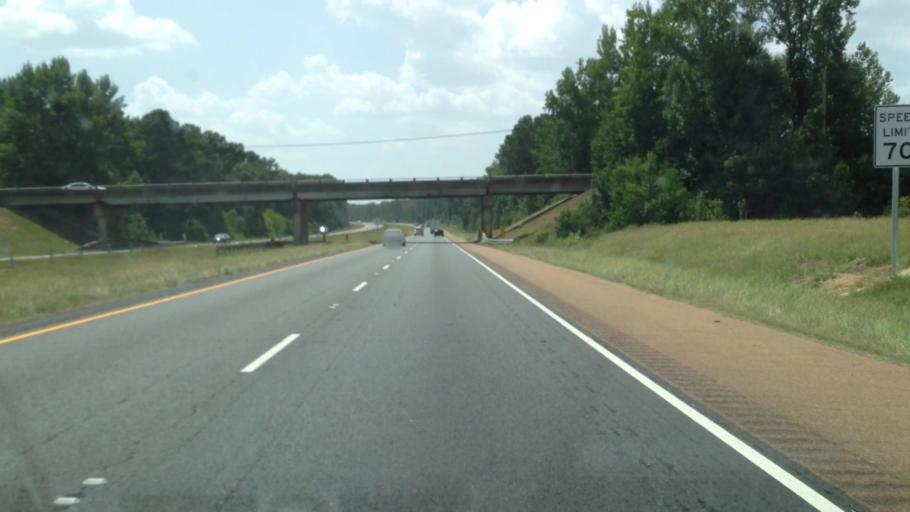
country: US
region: Louisiana
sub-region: Bienville Parish
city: Arcadia
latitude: 32.5657
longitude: -92.9198
